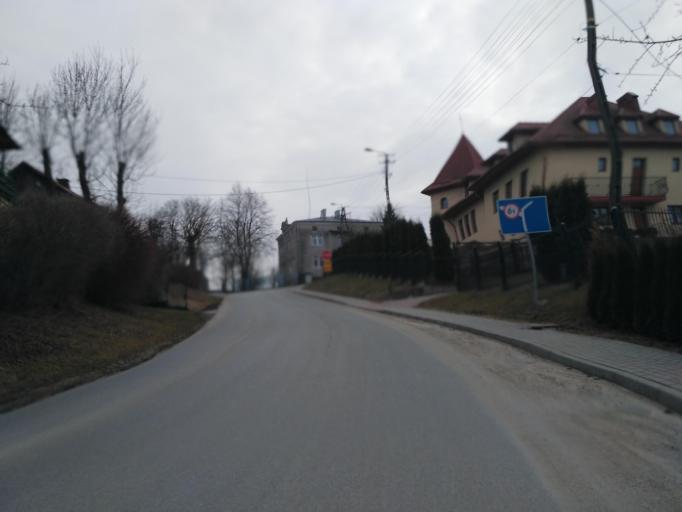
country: PL
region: Subcarpathian Voivodeship
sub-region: Powiat ropczycko-sedziszowski
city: Wielopole Skrzynskie
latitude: 49.9454
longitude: 21.6105
